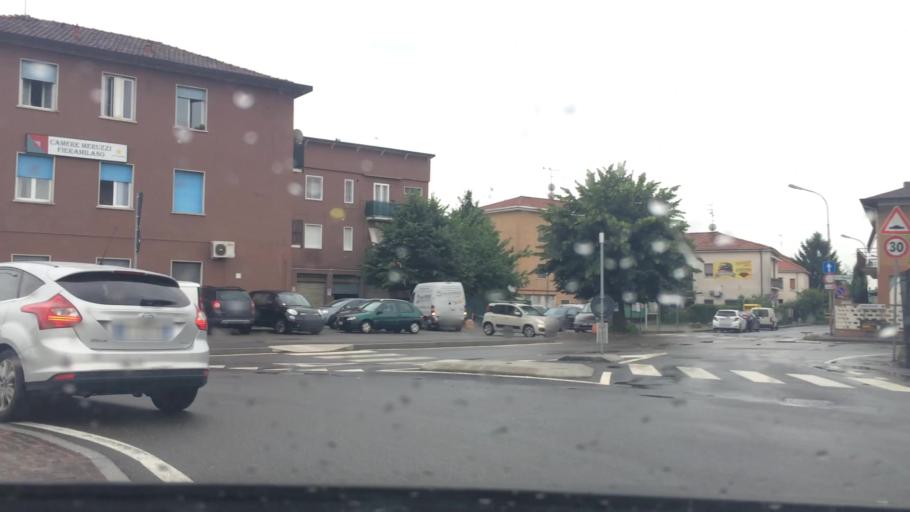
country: IT
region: Lombardy
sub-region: Citta metropolitana di Milano
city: Pero
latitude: 45.5184
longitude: 9.0708
